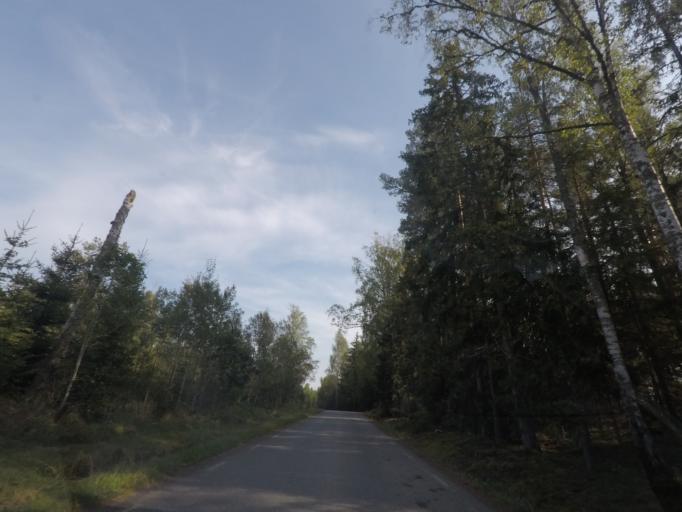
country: SE
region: Vaestmanland
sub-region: Kungsors Kommun
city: Kungsoer
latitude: 59.5111
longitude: 16.1506
